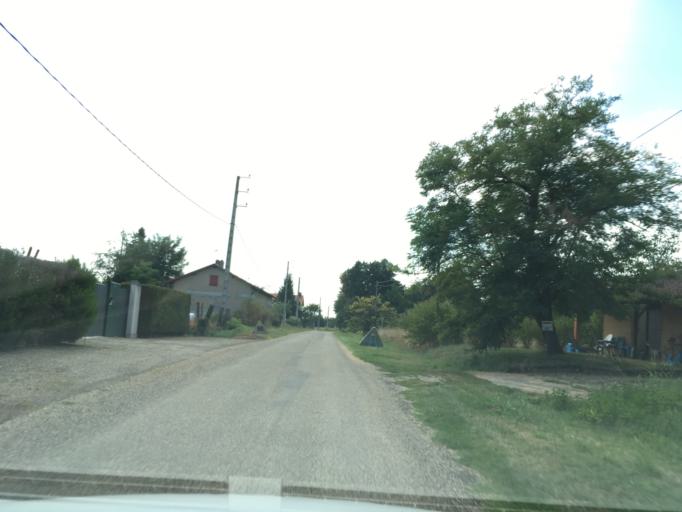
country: FR
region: Midi-Pyrenees
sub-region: Departement du Tarn-et-Garonne
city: Montbeton
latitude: 44.0152
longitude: 1.3152
